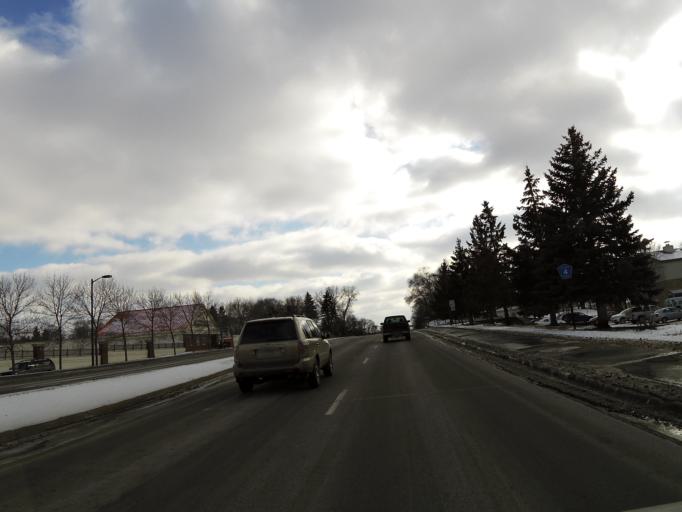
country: US
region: Minnesota
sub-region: Hennepin County
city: Eden Prairie
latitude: 44.8603
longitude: -93.4855
